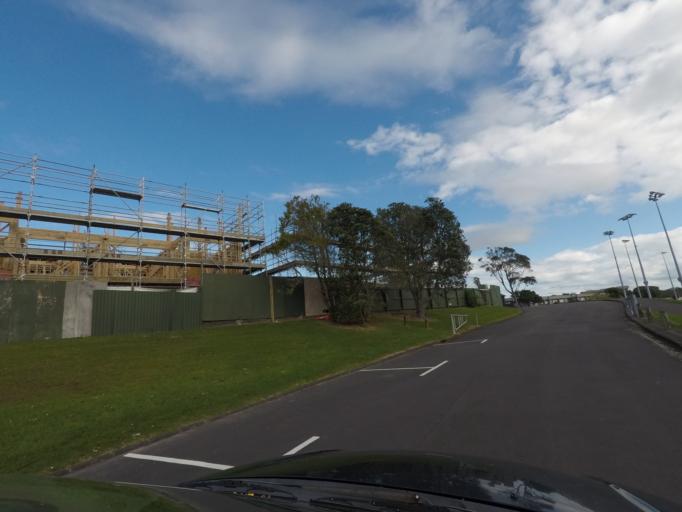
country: NZ
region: Auckland
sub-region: Auckland
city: Rosebank
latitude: -36.8722
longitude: 174.6440
